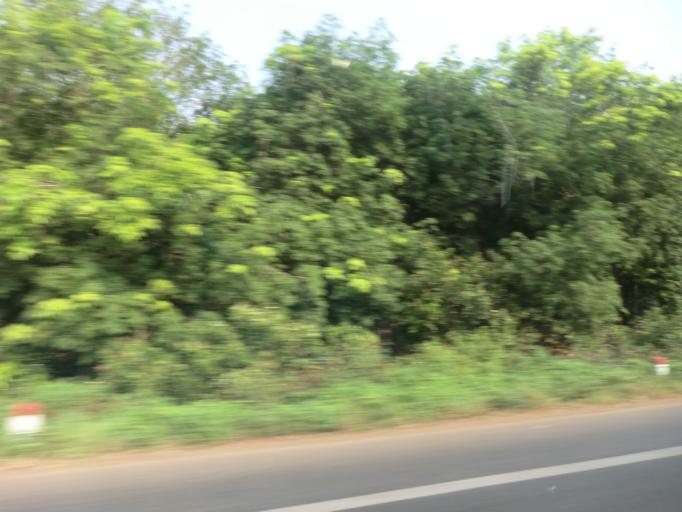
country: VN
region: Dong Nai
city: Thong Nhat
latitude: 11.0957
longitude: 107.2262
